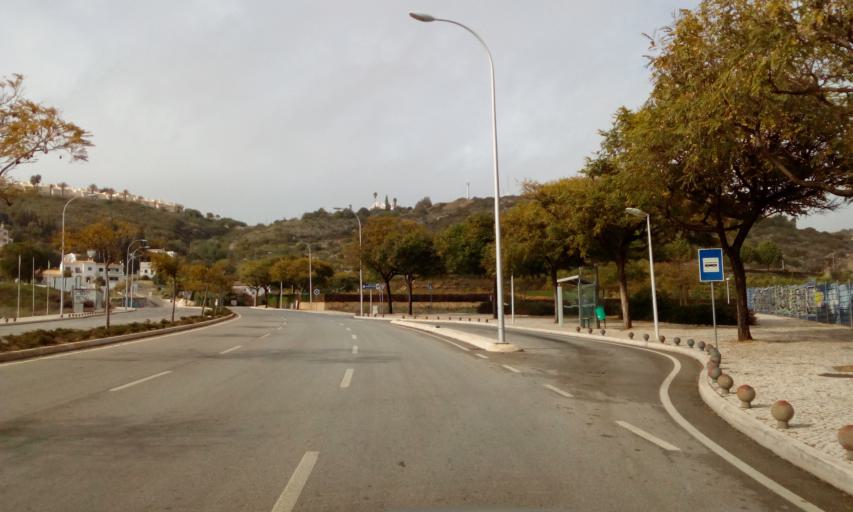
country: PT
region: Faro
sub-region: Albufeira
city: Albufeira
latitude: 37.0862
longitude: -8.2696
